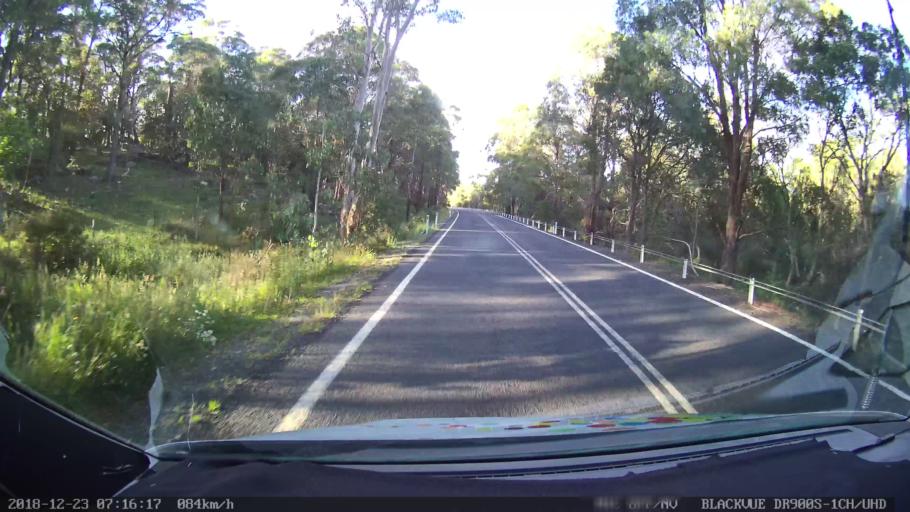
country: AU
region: New South Wales
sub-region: Bellingen
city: Dorrigo
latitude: -30.4542
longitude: 152.3103
